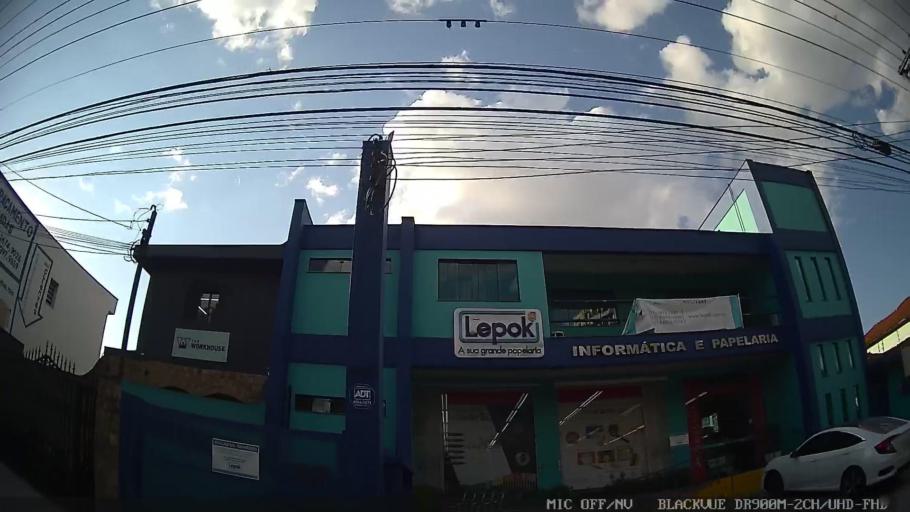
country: BR
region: Sao Paulo
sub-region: Sao Caetano Do Sul
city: Sao Caetano do Sul
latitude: -23.5637
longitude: -46.5432
